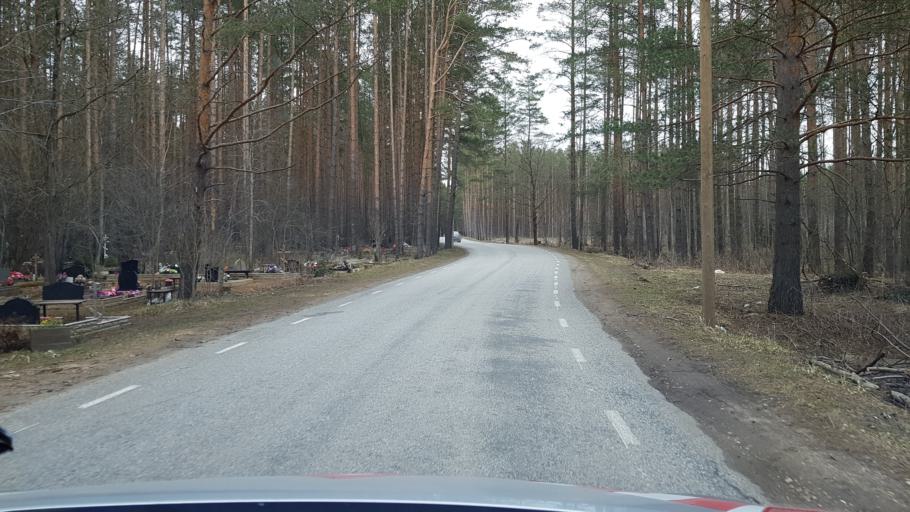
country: EE
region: Ida-Virumaa
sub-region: Narva-Joesuu linn
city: Narva-Joesuu
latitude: 59.4202
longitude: 28.1077
